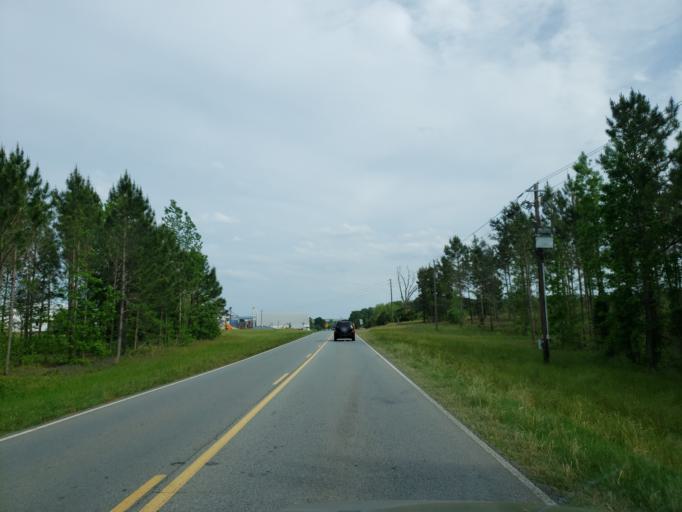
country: US
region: Georgia
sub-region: Dooly County
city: Vienna
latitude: 32.0993
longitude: -83.8134
